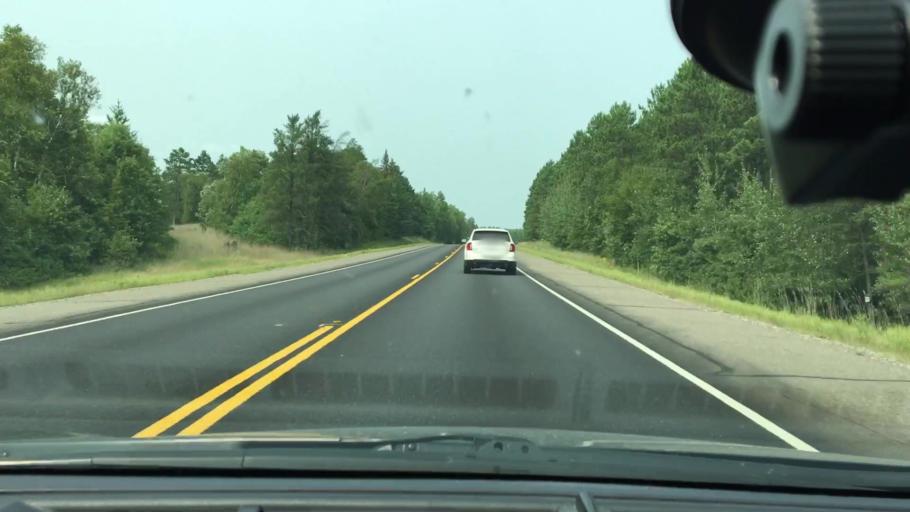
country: US
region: Minnesota
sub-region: Crow Wing County
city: Cross Lake
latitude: 46.6203
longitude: -94.1319
